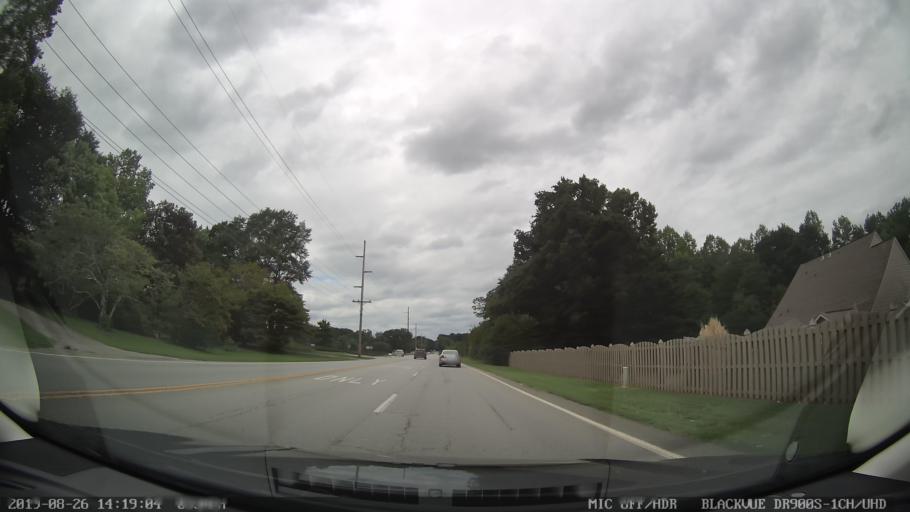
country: US
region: South Carolina
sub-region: Greenville County
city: Five Forks
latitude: 34.8011
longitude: -82.2391
